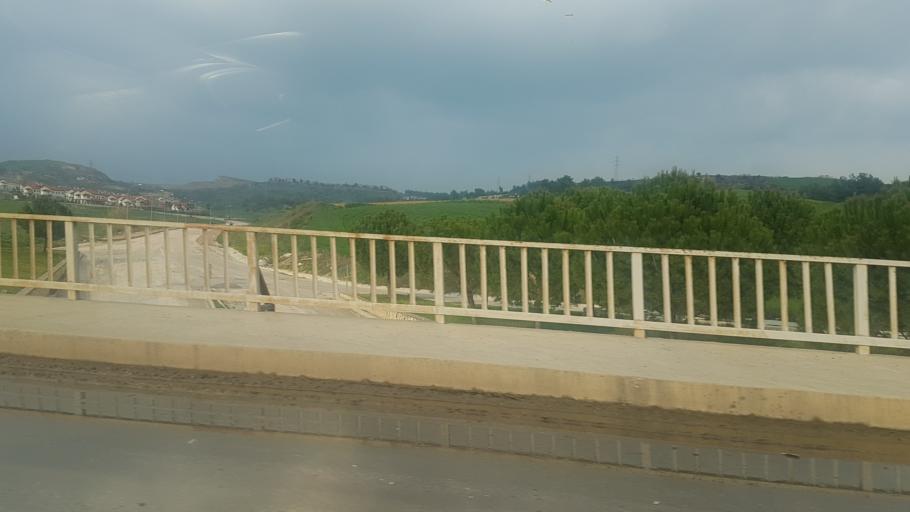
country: TR
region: Adana
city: Seyhan
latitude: 37.0474
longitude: 35.1789
